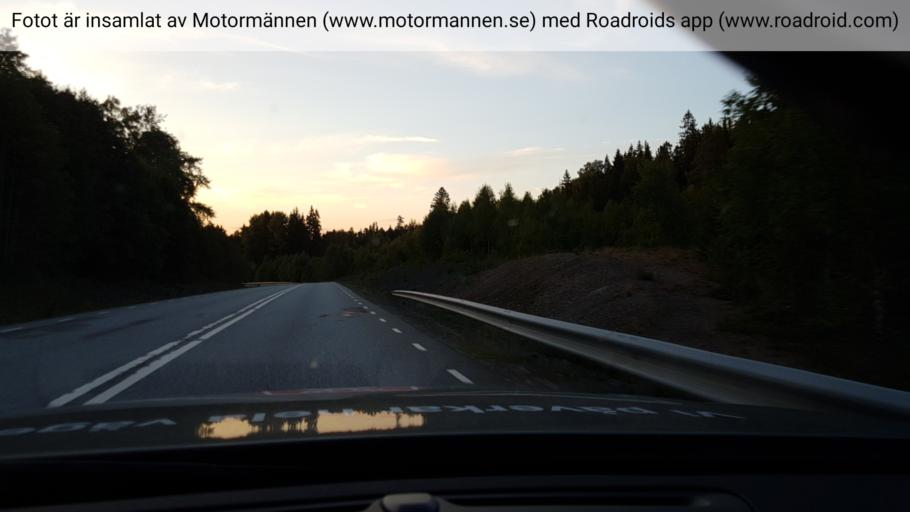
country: SE
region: OErebro
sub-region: Karlskoga Kommun
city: Karlskoga
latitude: 59.4500
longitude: 14.5090
